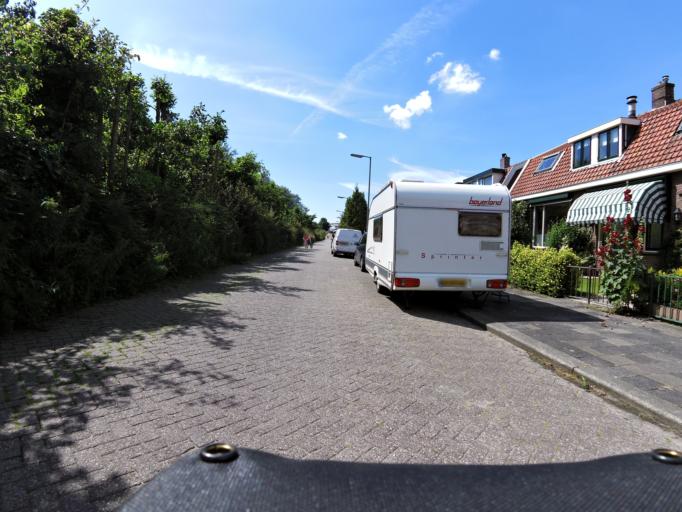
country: NL
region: South Holland
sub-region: Gemeente Albrandswaard
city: Rhoon
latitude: 51.8617
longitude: 4.3839
